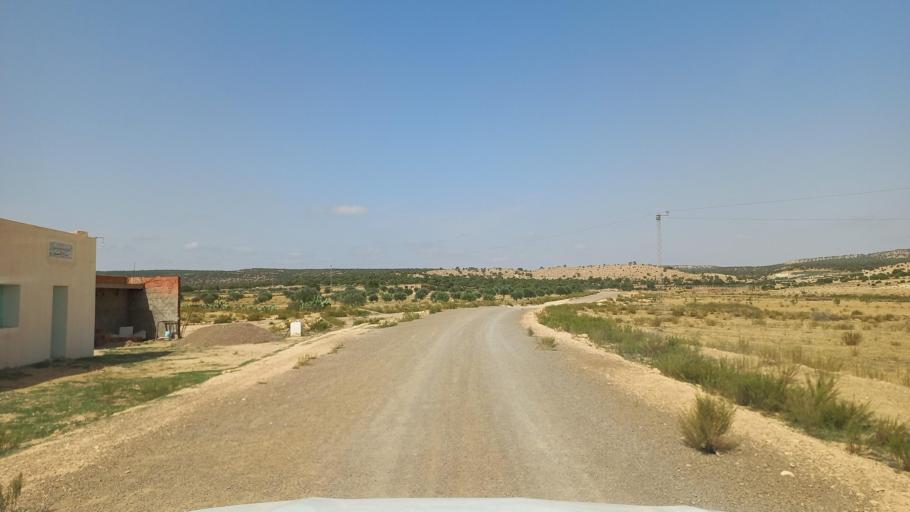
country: TN
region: Al Qasrayn
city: Sbiba
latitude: 35.3884
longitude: 8.9562
